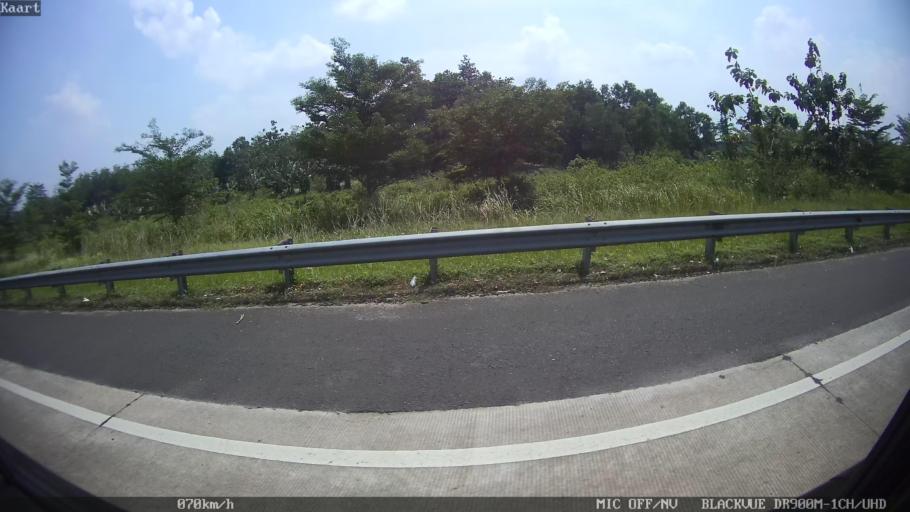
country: ID
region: Lampung
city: Kedaton
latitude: -5.3797
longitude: 105.3321
